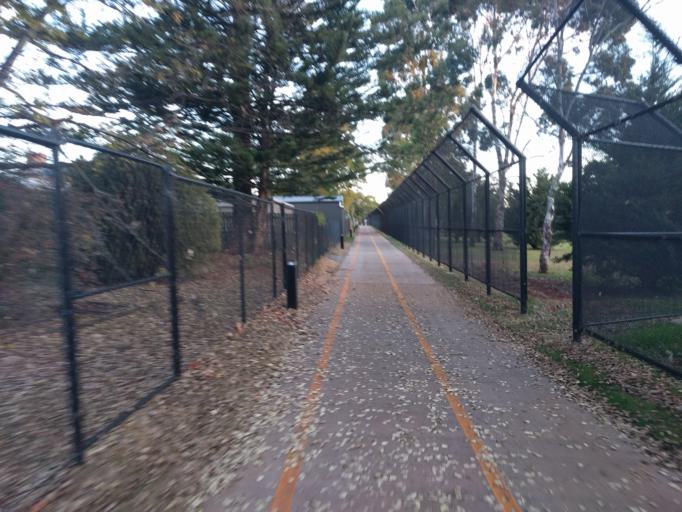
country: AU
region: Queensland
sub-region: Toowoomba
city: Toowoomba
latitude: -27.5790
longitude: 151.9480
